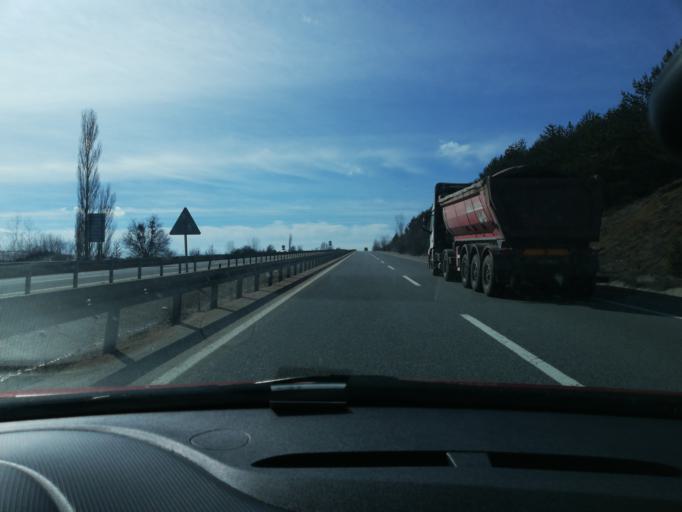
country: TR
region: Bolu
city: Gerede
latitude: 40.8266
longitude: 32.3536
